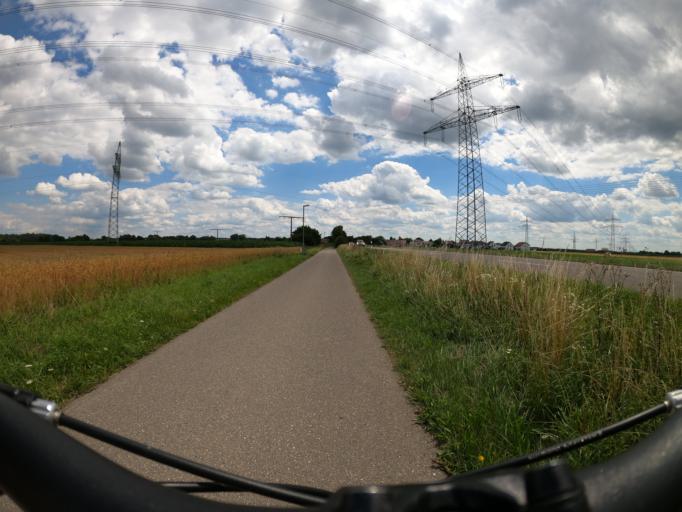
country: DE
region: Bavaria
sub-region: Swabia
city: Nersingen
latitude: 48.4217
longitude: 10.1301
